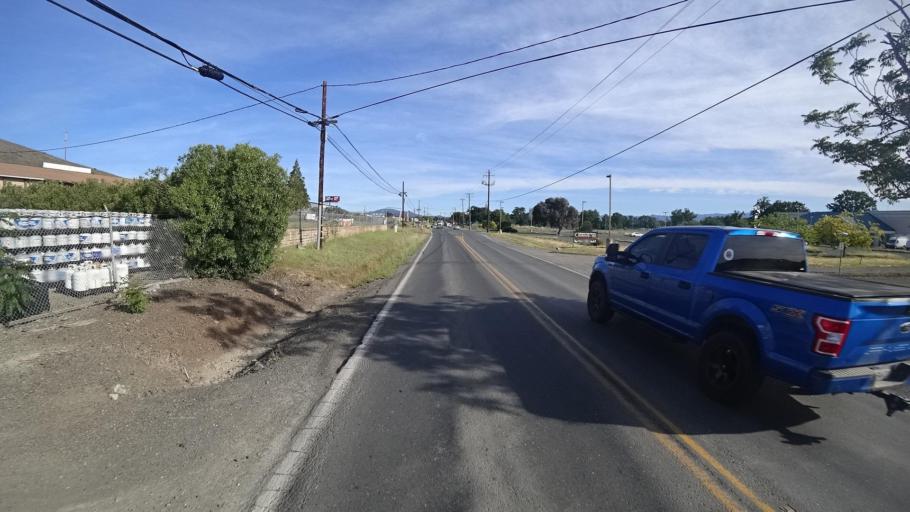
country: US
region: California
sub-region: Lake County
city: Lakeport
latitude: 39.0143
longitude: -122.9099
